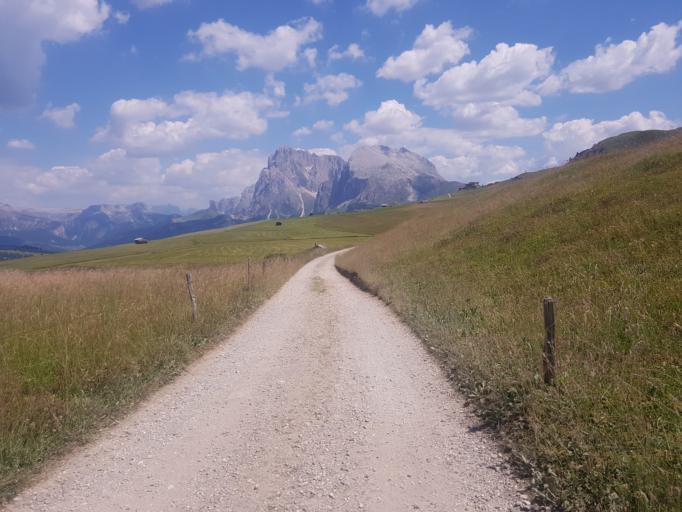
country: IT
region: Trentino-Alto Adige
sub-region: Bolzano
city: Siusi
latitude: 46.5248
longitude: 11.6234
